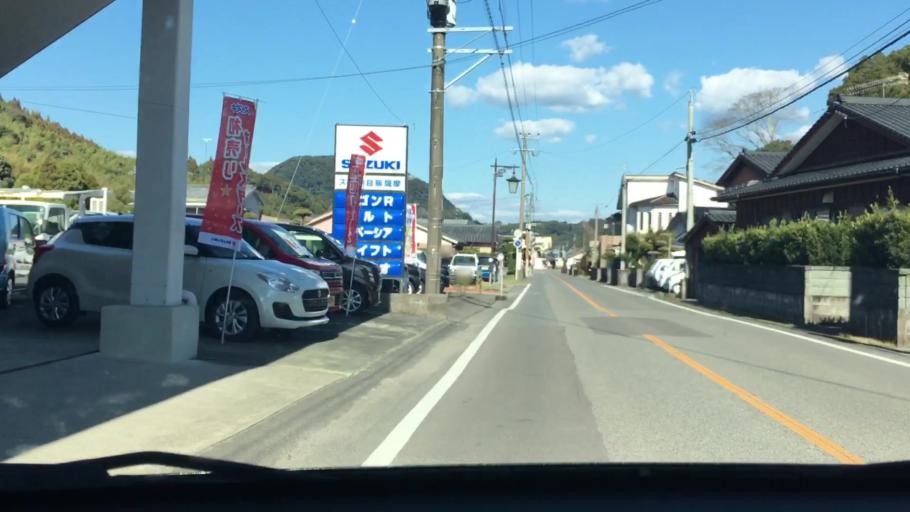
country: JP
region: Kagoshima
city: Satsumasendai
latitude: 31.7857
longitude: 130.4027
